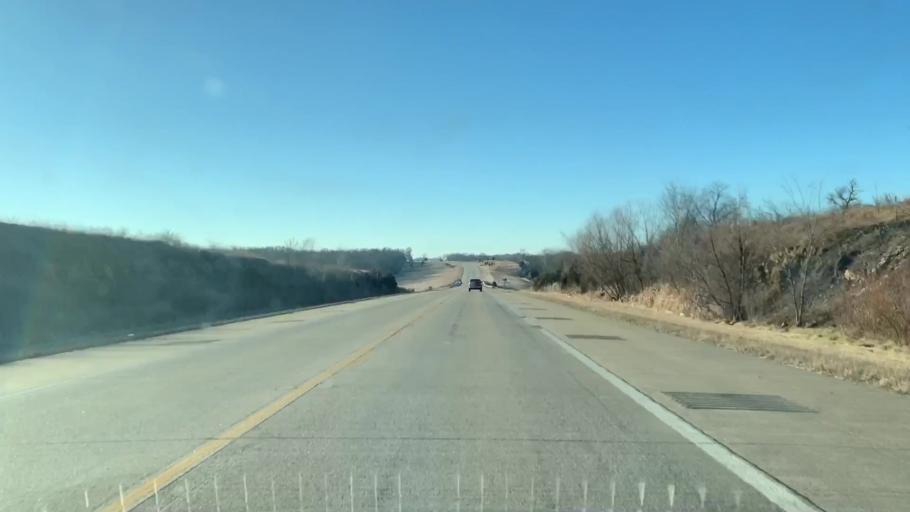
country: US
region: Kansas
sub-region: Crawford County
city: Arma
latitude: 37.5876
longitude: -94.7055
